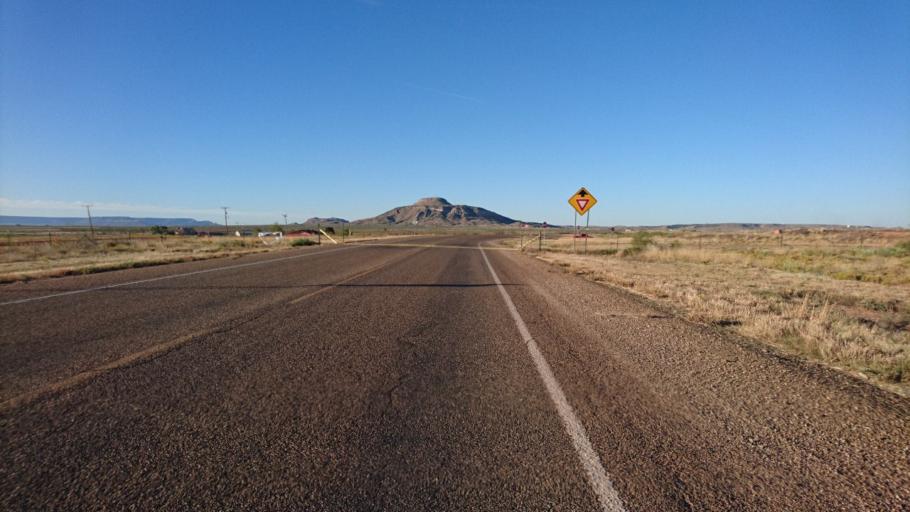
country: US
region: New Mexico
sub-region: Quay County
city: Tucumcari
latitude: 35.1685
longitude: -103.6727
